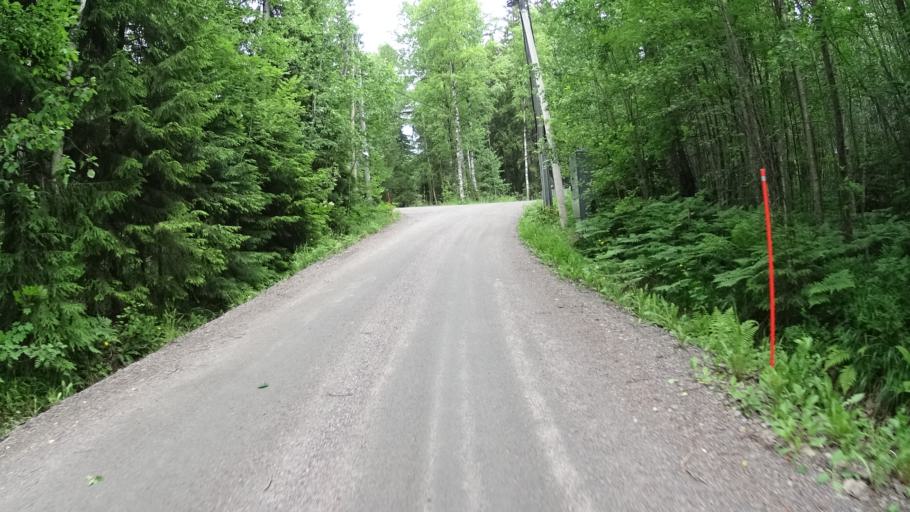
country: FI
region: Uusimaa
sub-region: Helsinki
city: Espoo
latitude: 60.2877
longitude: 24.5135
